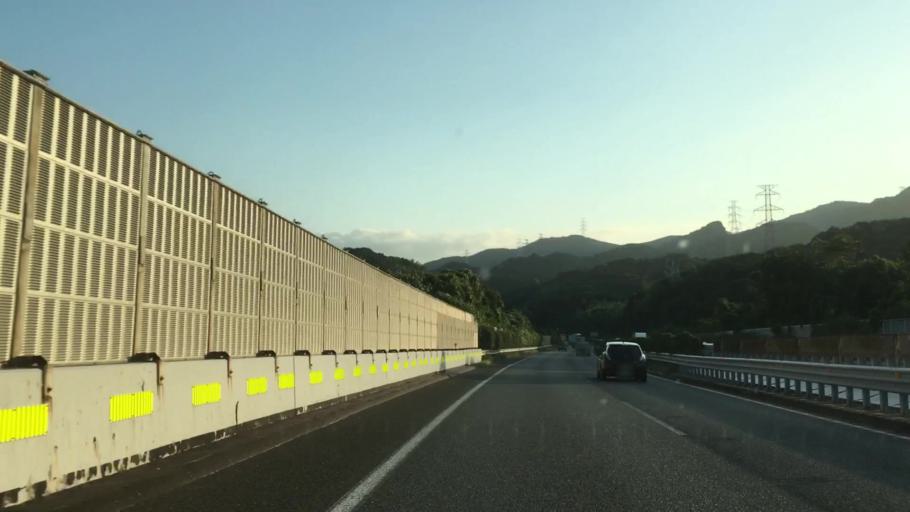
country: JP
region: Yamaguchi
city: Shimonoseki
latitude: 33.9091
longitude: 130.9745
